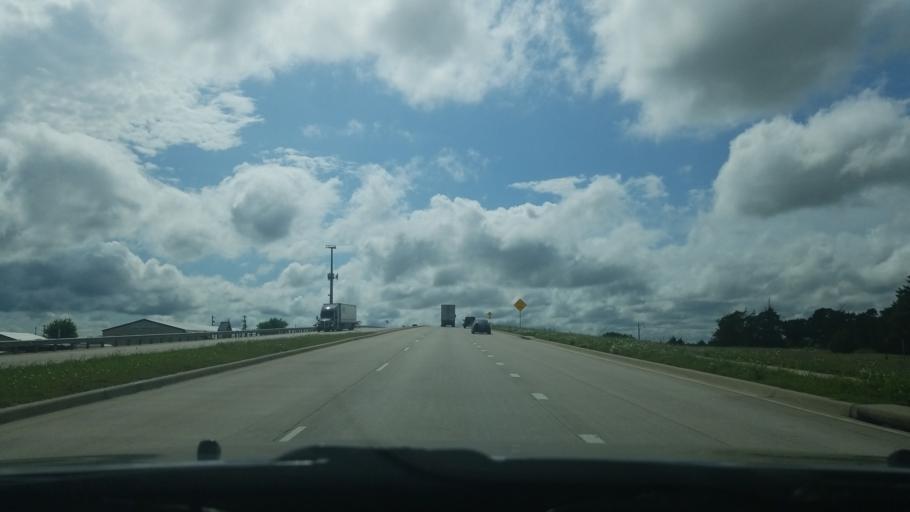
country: US
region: Texas
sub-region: Denton County
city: Krum
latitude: 33.2347
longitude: -97.2456
